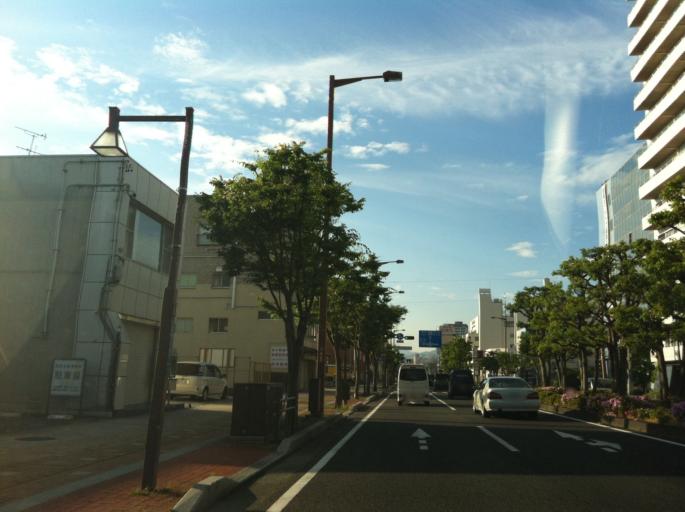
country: JP
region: Shizuoka
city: Shizuoka-shi
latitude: 35.0116
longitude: 138.4891
